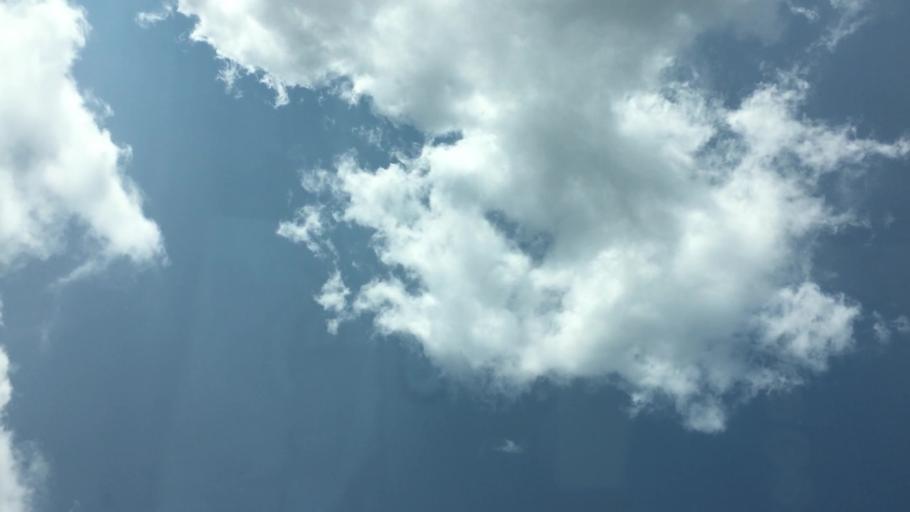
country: US
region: Alabama
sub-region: Pickens County
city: Gordo
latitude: 33.2747
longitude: -87.7599
